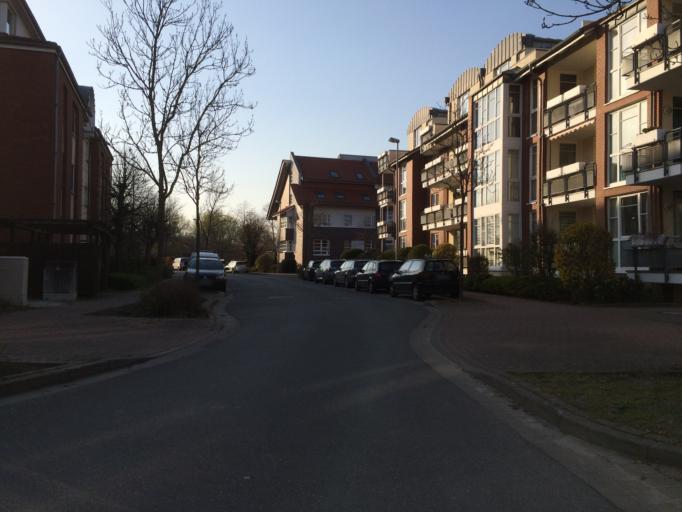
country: DE
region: Lower Saxony
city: Gehrden
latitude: 52.3086
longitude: 9.6136
